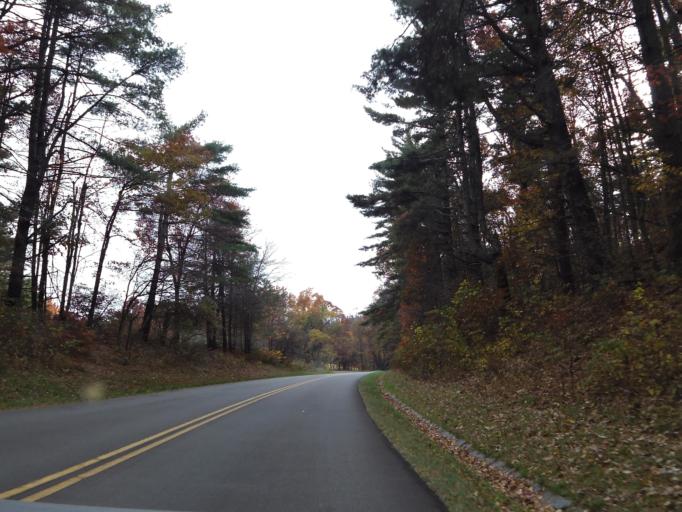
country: US
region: North Carolina
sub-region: Ashe County
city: Jefferson
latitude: 36.3402
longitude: -81.3730
